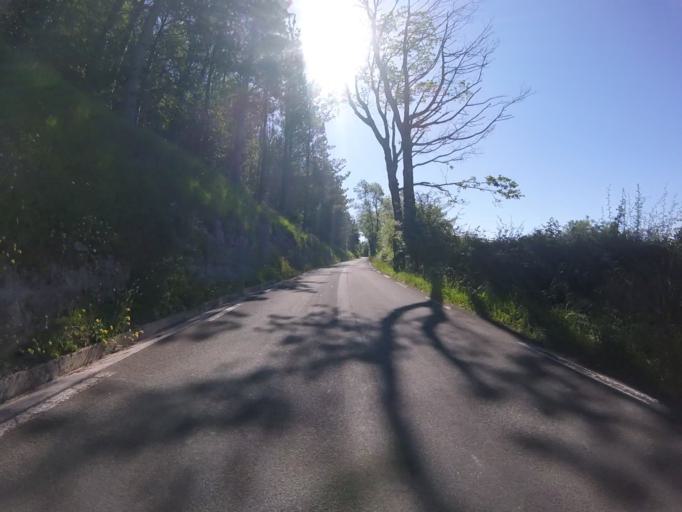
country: ES
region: Basque Country
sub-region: Provincia de Guipuzcoa
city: Beizama
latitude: 43.1244
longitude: -2.1927
